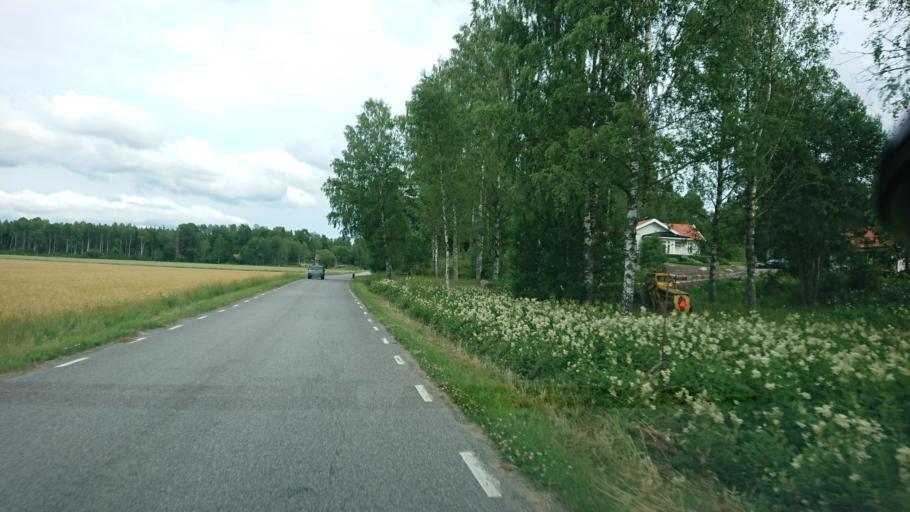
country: SE
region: Uppsala
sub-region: Osthammars Kommun
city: Bjorklinge
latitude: 60.0010
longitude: 17.4667
